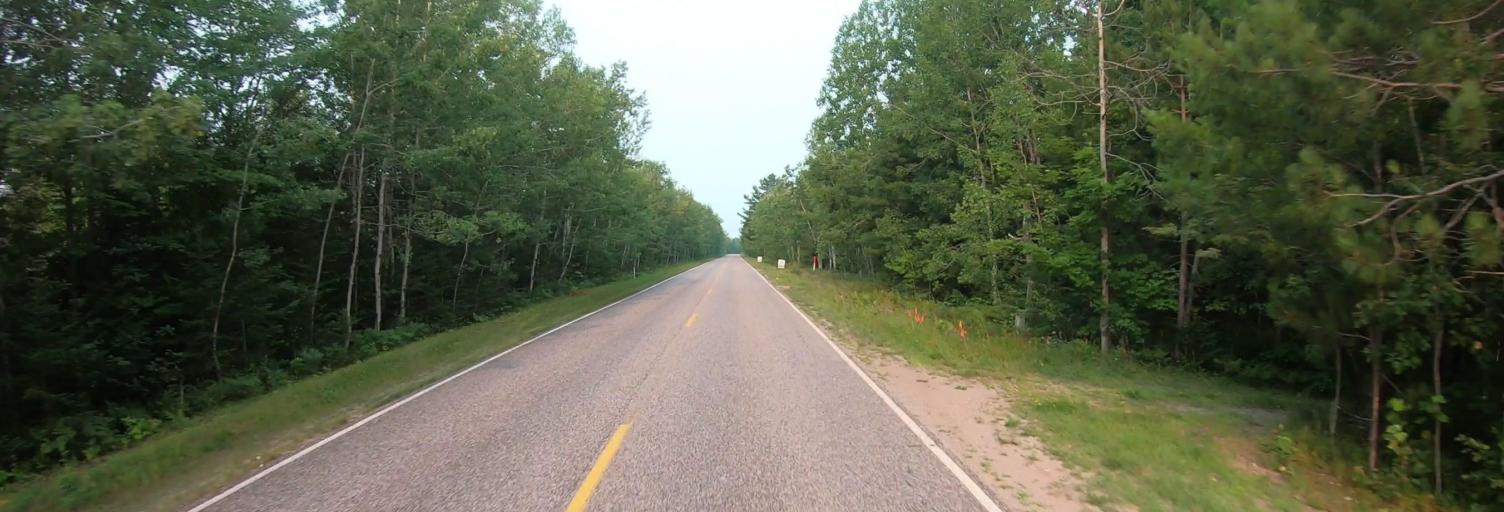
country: US
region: Michigan
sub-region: Chippewa County
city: Sault Ste. Marie
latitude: 46.4652
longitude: -84.8828
